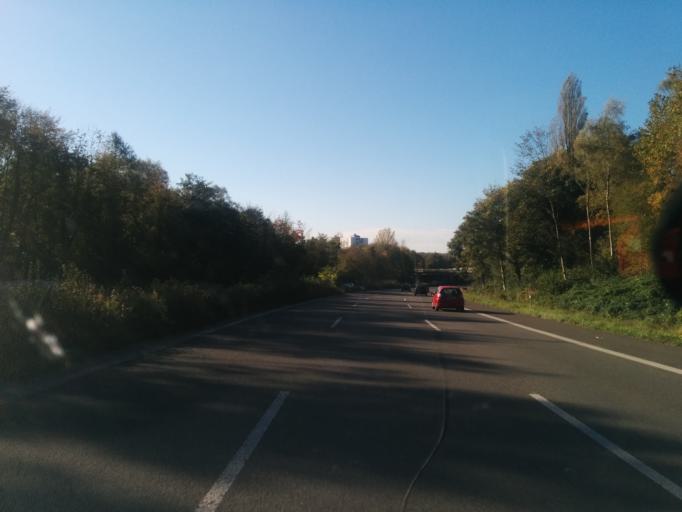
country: DE
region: North Rhine-Westphalia
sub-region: Regierungsbezirk Dusseldorf
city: Essen
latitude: 51.4347
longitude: 7.0261
